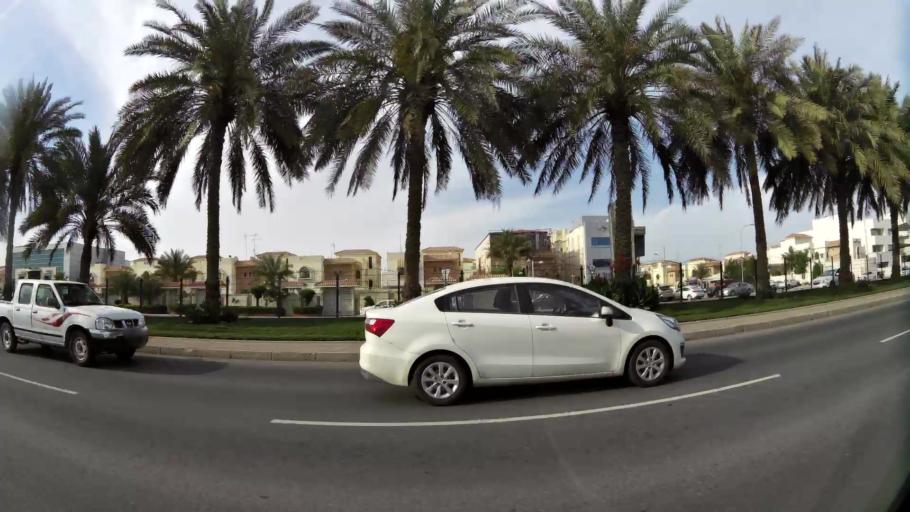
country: QA
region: Baladiyat ad Dawhah
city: Doha
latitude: 25.2543
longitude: 51.5302
